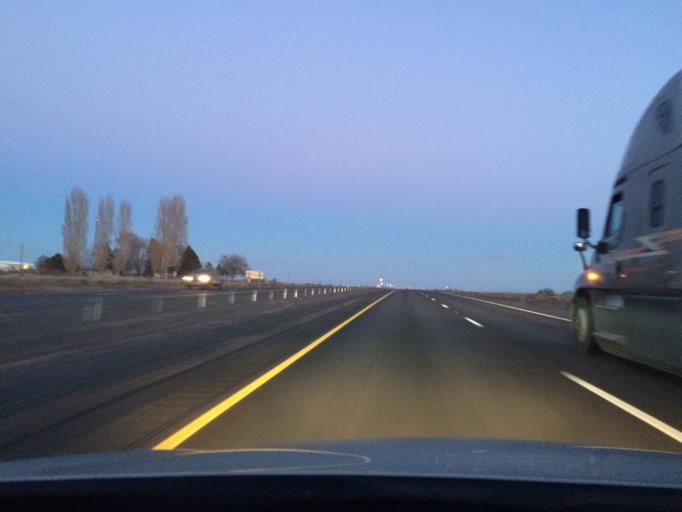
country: US
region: Washington
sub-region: Grant County
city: Royal City
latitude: 47.1038
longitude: -119.6088
